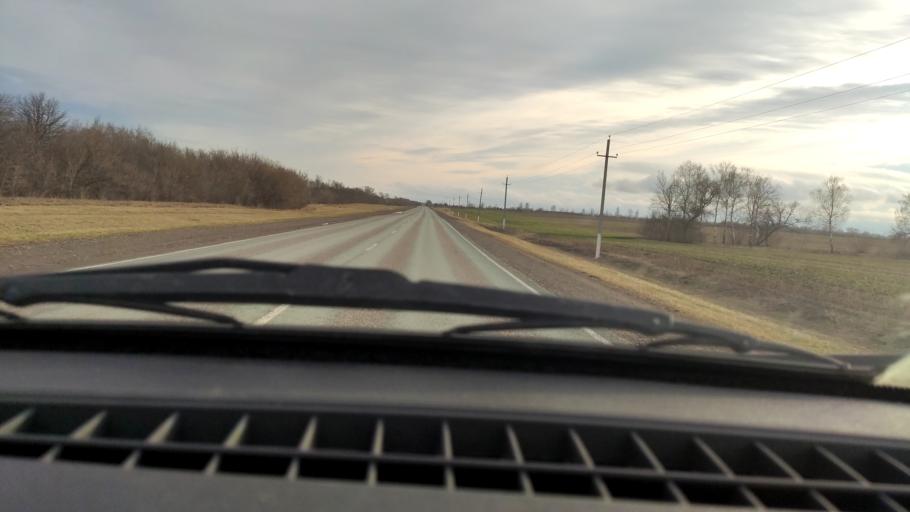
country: RU
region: Bashkortostan
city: Davlekanovo
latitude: 54.3101
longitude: 55.1433
